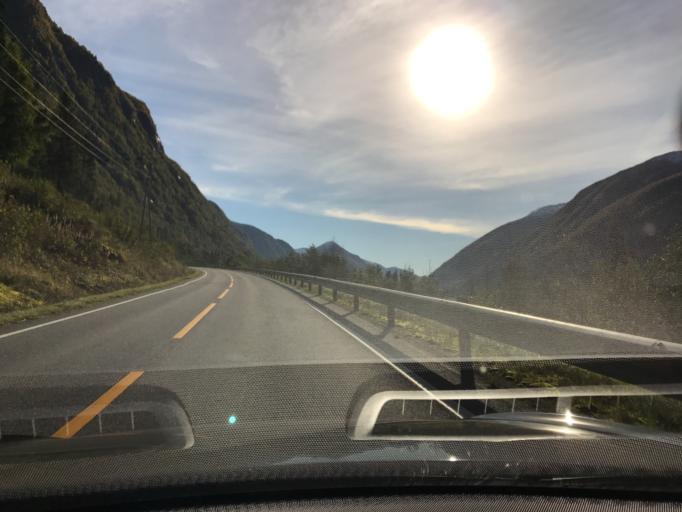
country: NO
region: Sogn og Fjordane
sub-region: Leikanger
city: Hermansverk
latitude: 61.4104
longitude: 6.7597
